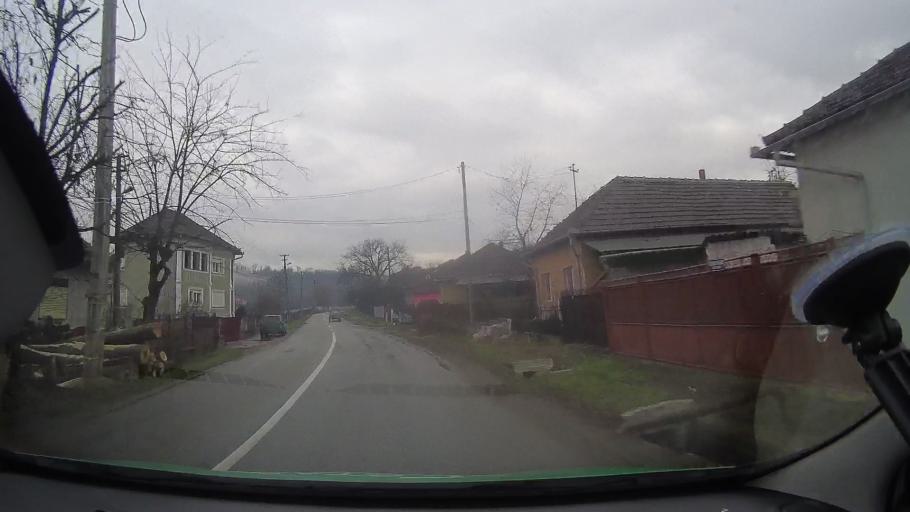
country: RO
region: Arad
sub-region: Comuna Gurahont
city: Gurahont
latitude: 46.2671
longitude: 22.3423
